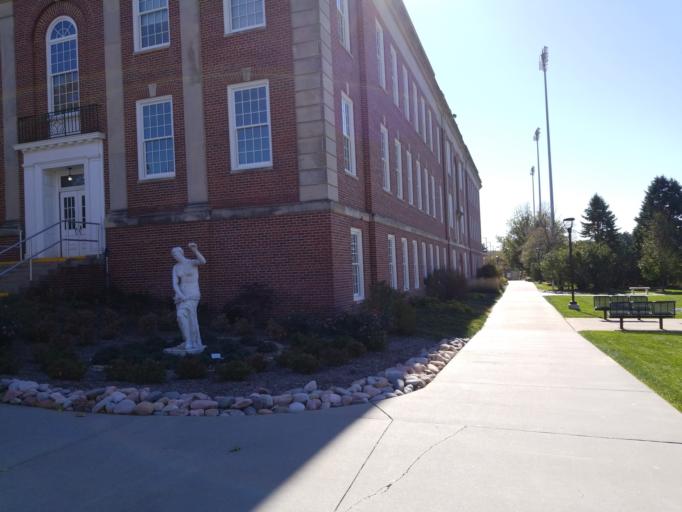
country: US
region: Nebraska
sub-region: Douglas County
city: Ralston
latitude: 41.2584
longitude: -96.0065
